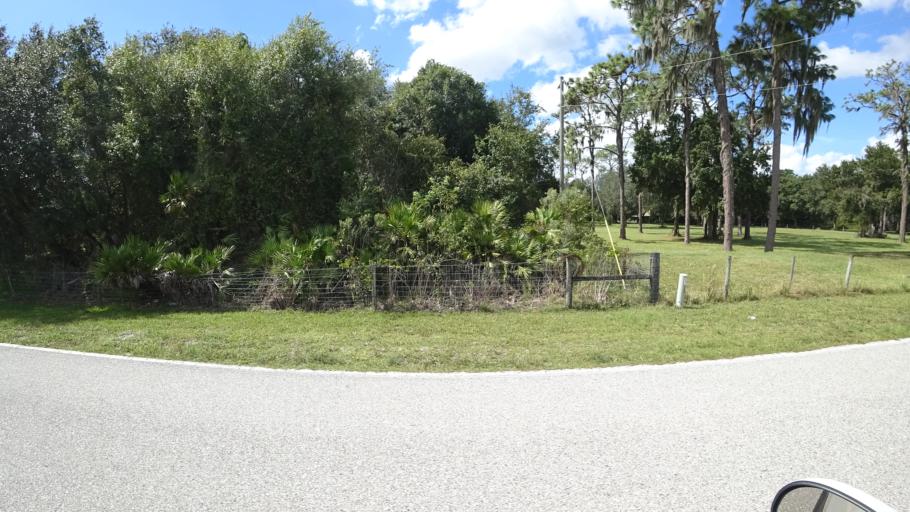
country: US
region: Florida
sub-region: Sarasota County
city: Lake Sarasota
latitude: 27.3308
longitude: -82.1668
